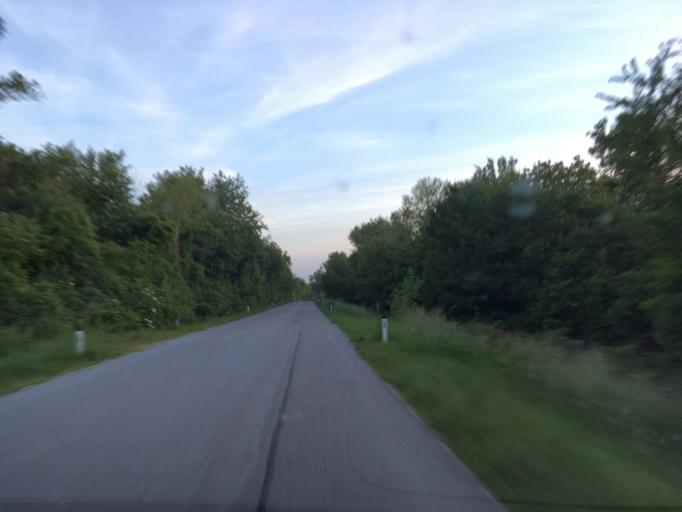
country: AT
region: Lower Austria
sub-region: Politischer Bezirk Mistelbach
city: Herrnbaumgarten
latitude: 48.7174
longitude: 16.6717
